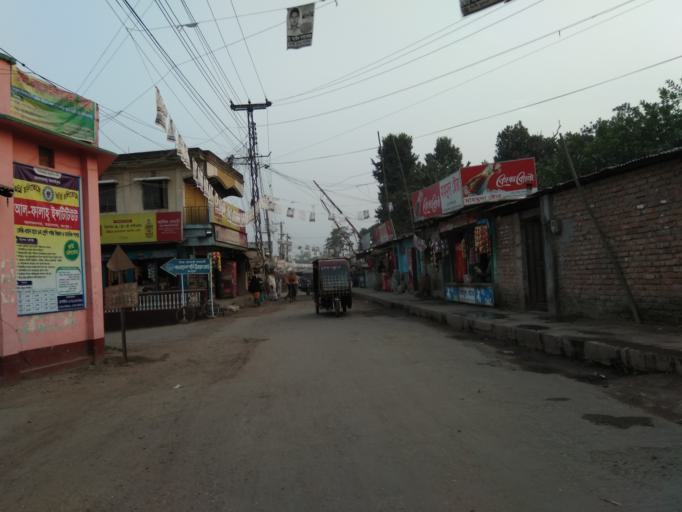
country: BD
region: Rangpur Division
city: Rangpur
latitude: 25.7296
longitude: 89.2665
